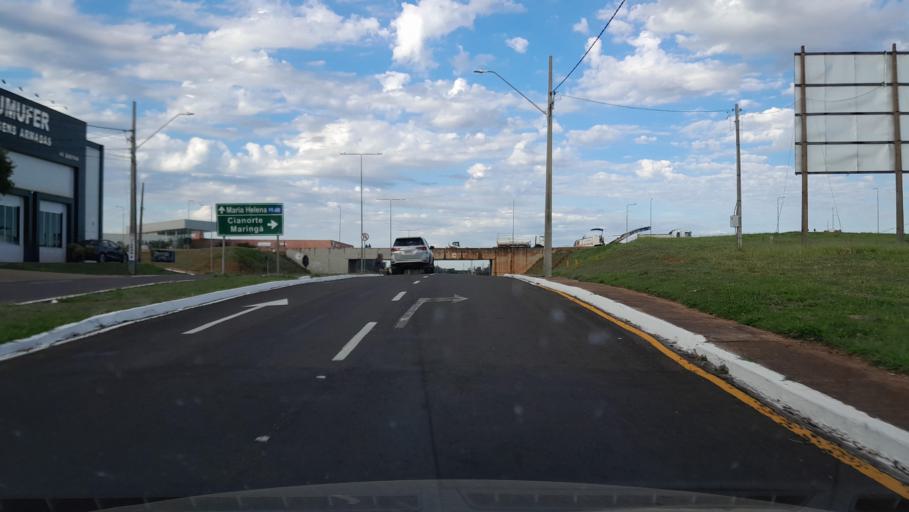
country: BR
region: Parana
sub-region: Umuarama
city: Umuarama
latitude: -23.7525
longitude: -53.2737
